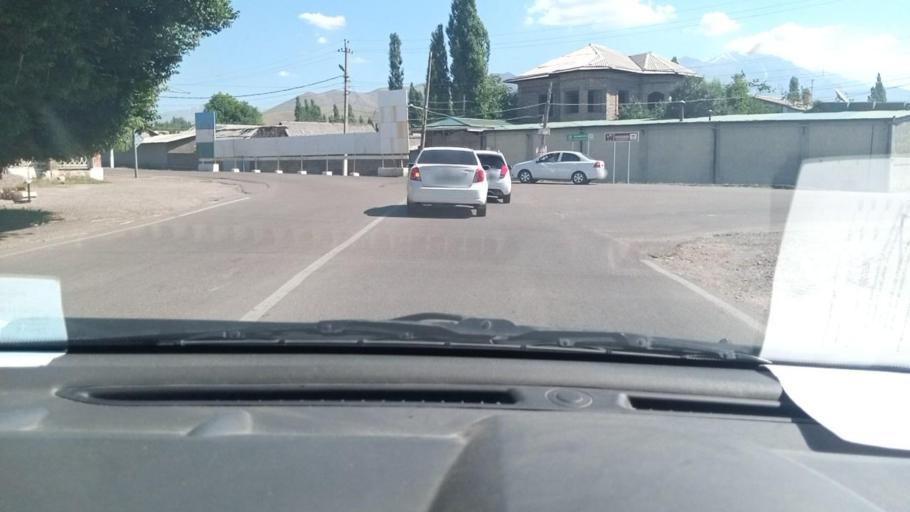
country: UZ
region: Toshkent
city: Angren
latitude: 41.0385
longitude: 70.0942
